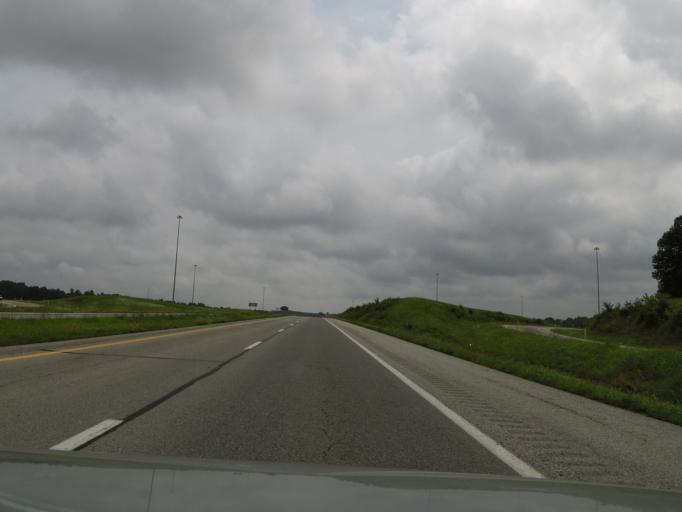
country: US
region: Kentucky
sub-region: Ohio County
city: Beaver Dam
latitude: 37.3823
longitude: -86.8134
